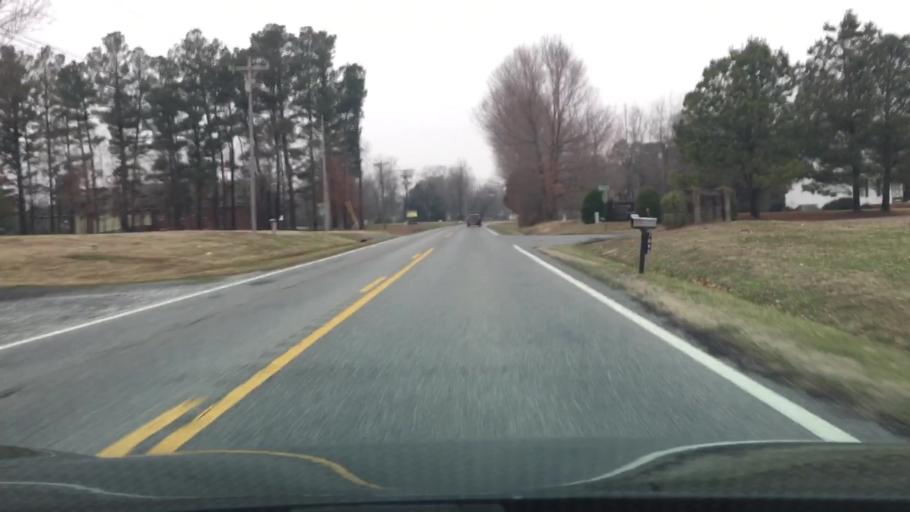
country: US
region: Kentucky
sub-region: Livingston County
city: Ledbetter
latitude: 36.9679
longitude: -88.4549
